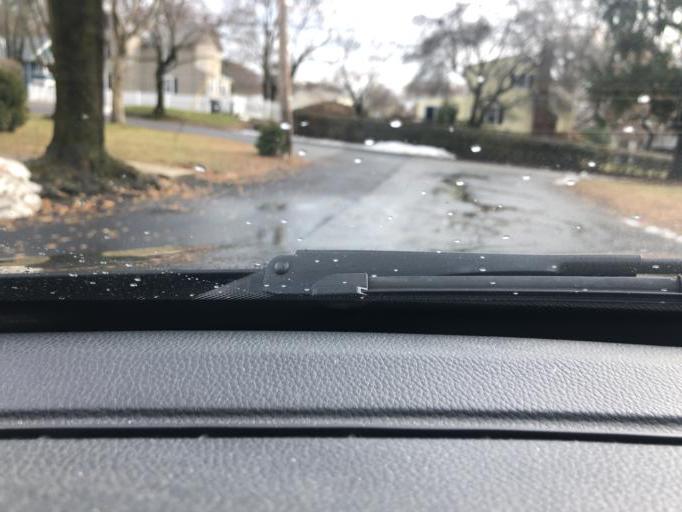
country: US
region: Massachusetts
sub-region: Middlesex County
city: Arlington
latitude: 42.4248
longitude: -71.1675
